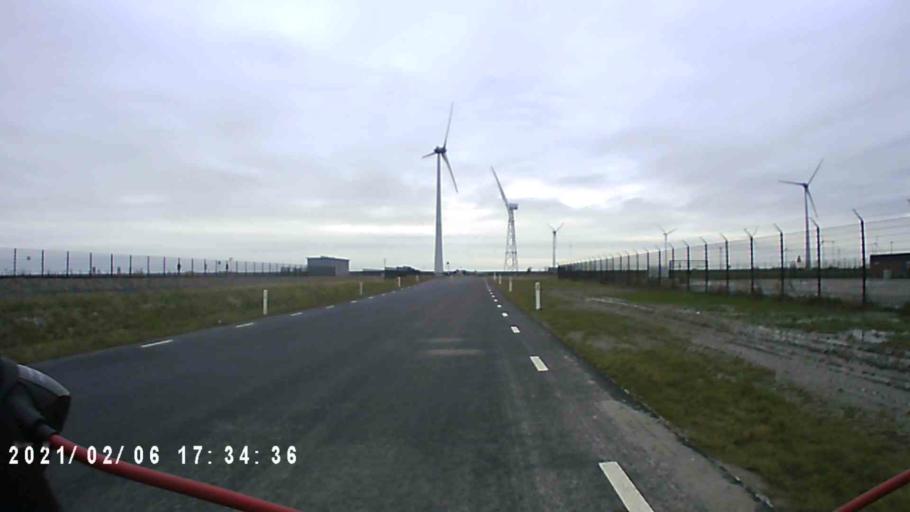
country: NL
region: Groningen
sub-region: Gemeente Appingedam
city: Appingedam
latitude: 53.4488
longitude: 6.7933
